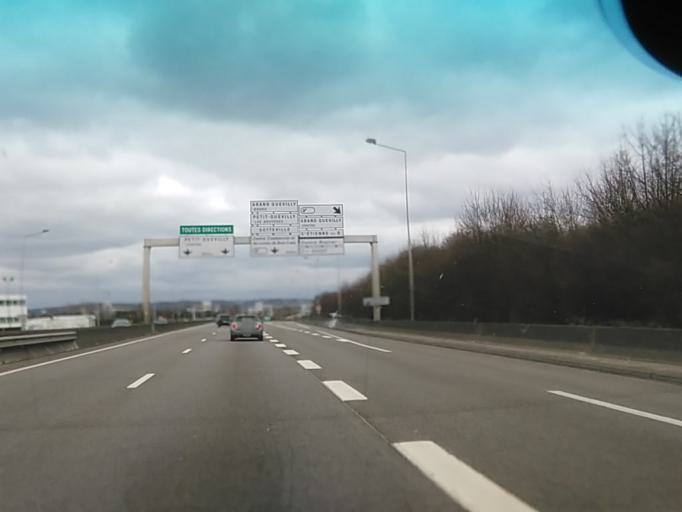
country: FR
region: Haute-Normandie
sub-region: Departement de la Seine-Maritime
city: Le Grand-Quevilly
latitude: 49.4053
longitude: 1.0353
